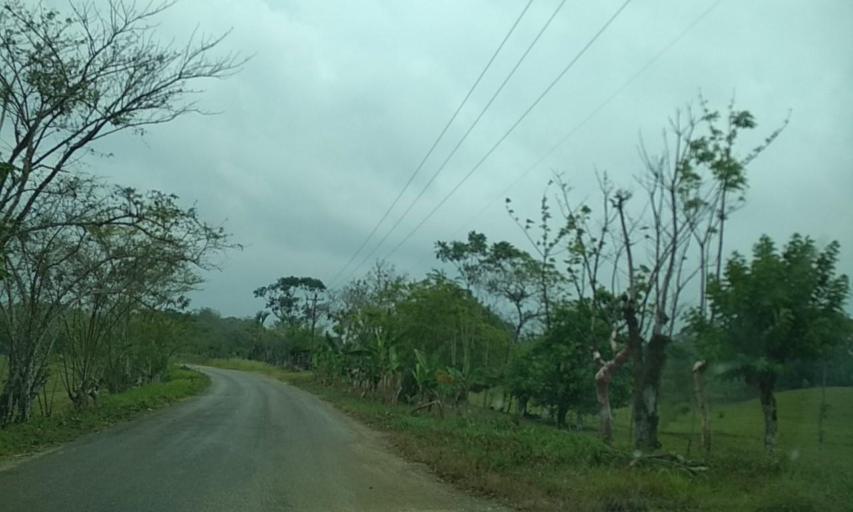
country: MX
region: Tabasco
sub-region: Huimanguillo
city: Francisco Rueda
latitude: 17.5837
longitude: -94.0923
